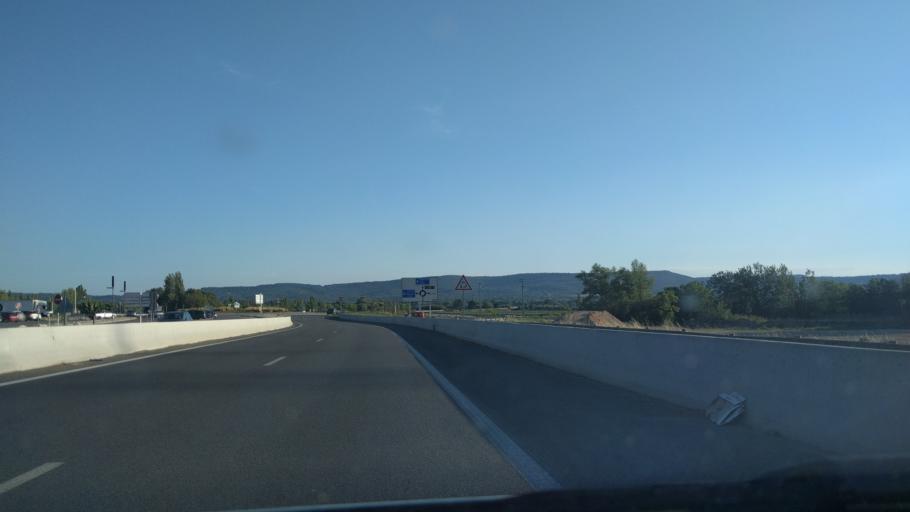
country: FR
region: Provence-Alpes-Cote d'Azur
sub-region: Departement du Vaucluse
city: Pertuis
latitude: 43.6645
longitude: 5.4954
